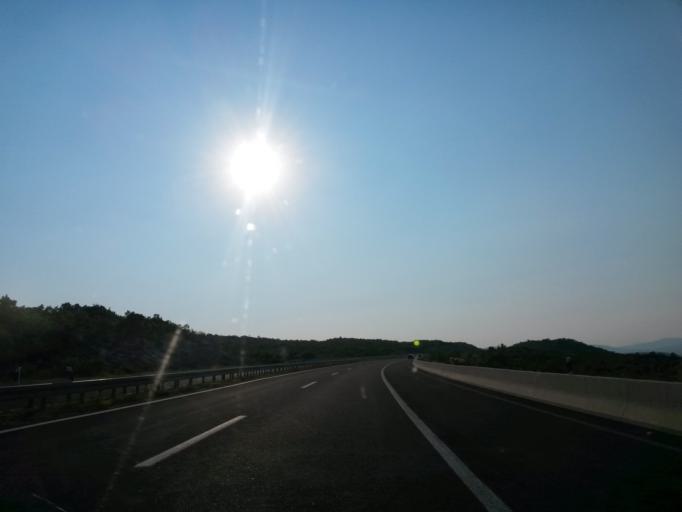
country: HR
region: Splitsko-Dalmatinska
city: Dugopolje
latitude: 43.5826
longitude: 16.6470
